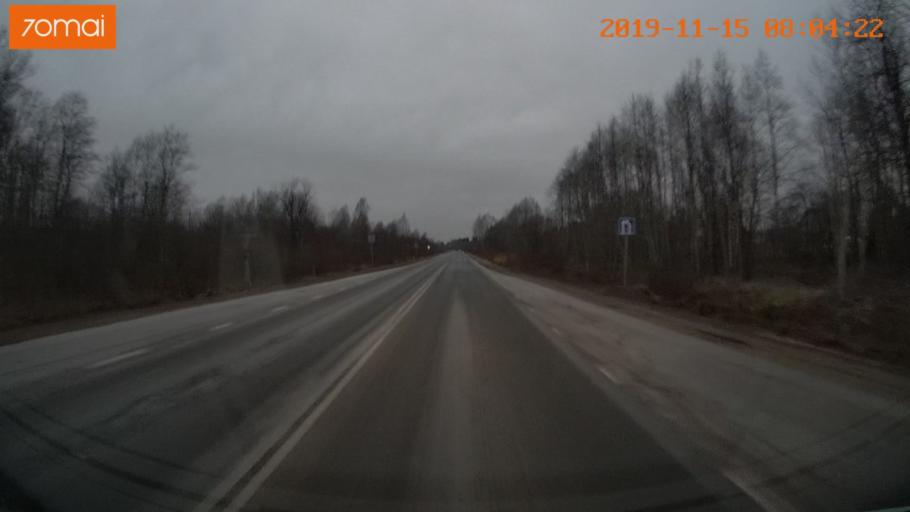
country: RU
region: Vologda
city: Cherepovets
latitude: 59.0076
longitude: 38.0772
